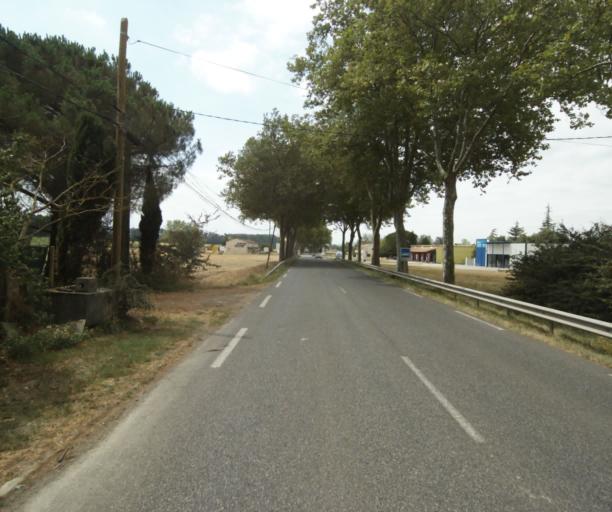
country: FR
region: Midi-Pyrenees
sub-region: Departement de la Haute-Garonne
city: Revel
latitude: 43.4481
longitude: 1.9642
